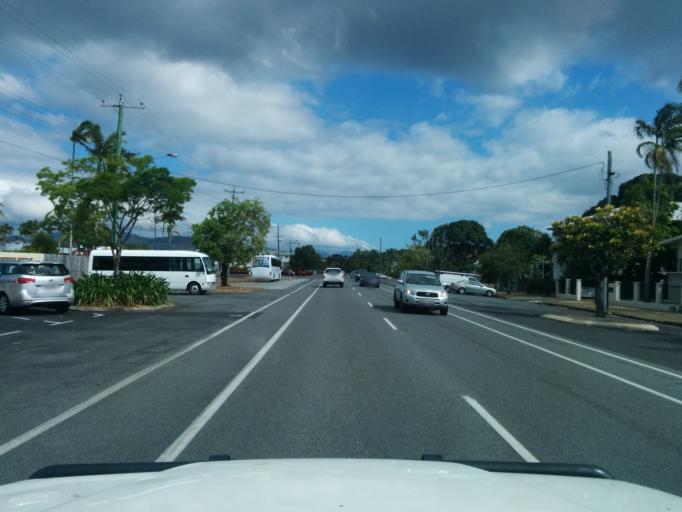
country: AU
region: Queensland
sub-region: Cairns
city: Cairns
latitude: -16.9117
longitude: 145.7621
